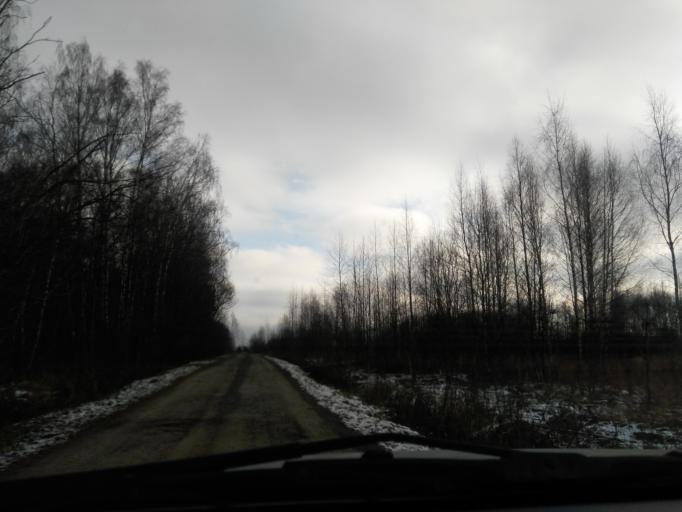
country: RU
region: Moskovskaya
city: Troitsk
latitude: 55.3692
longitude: 37.1684
